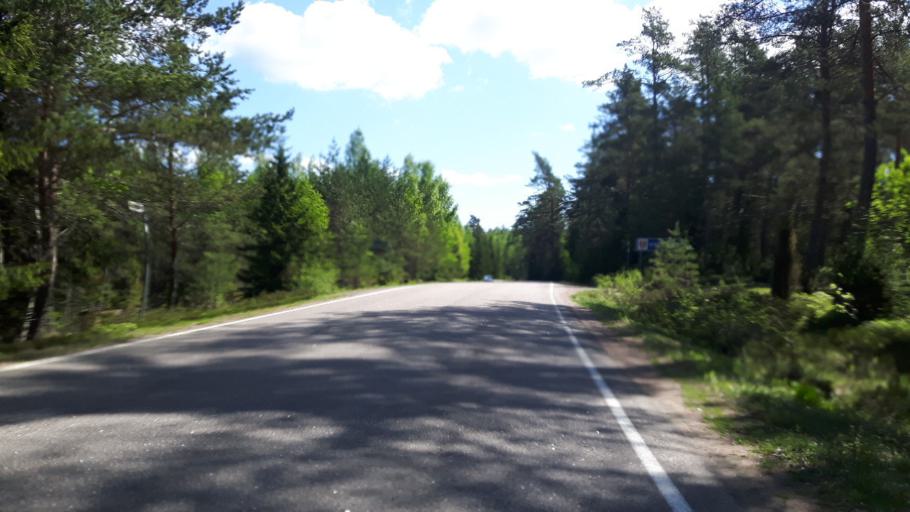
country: FI
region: Kymenlaakso
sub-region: Kotka-Hamina
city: Hamina
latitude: 60.5118
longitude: 27.3975
